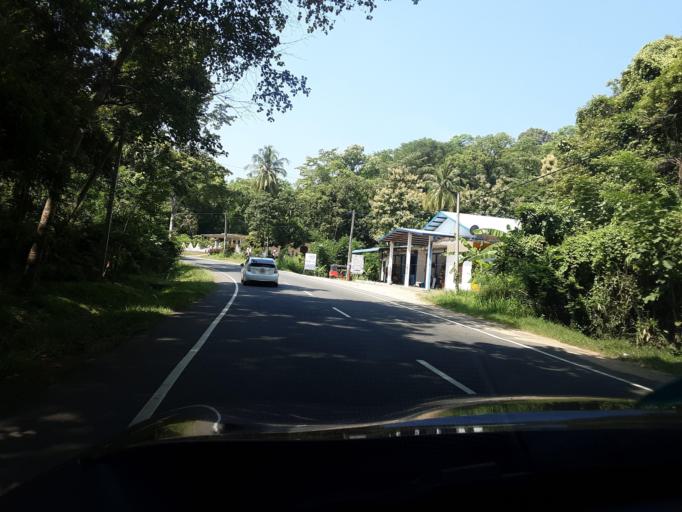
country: LK
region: Uva
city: Badulla
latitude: 7.2838
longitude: 81.0335
